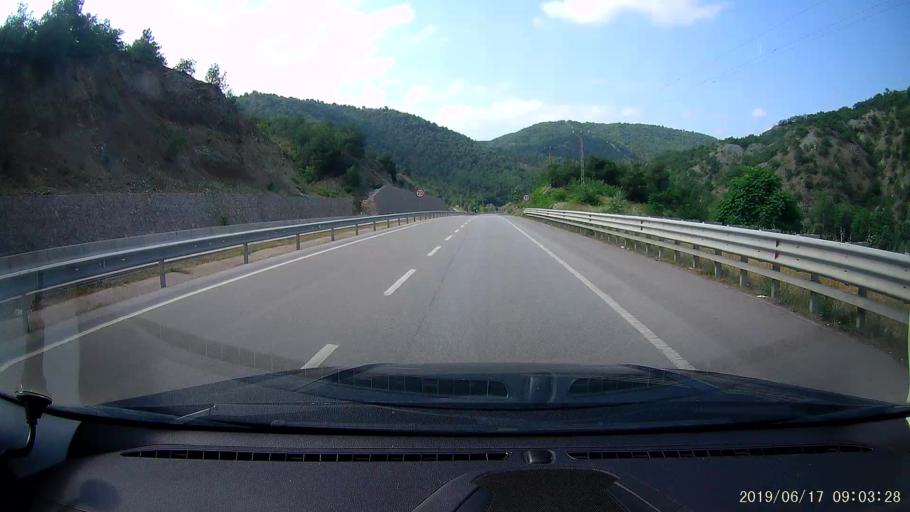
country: TR
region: Amasya
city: Tasova
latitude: 40.7551
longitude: 36.3023
